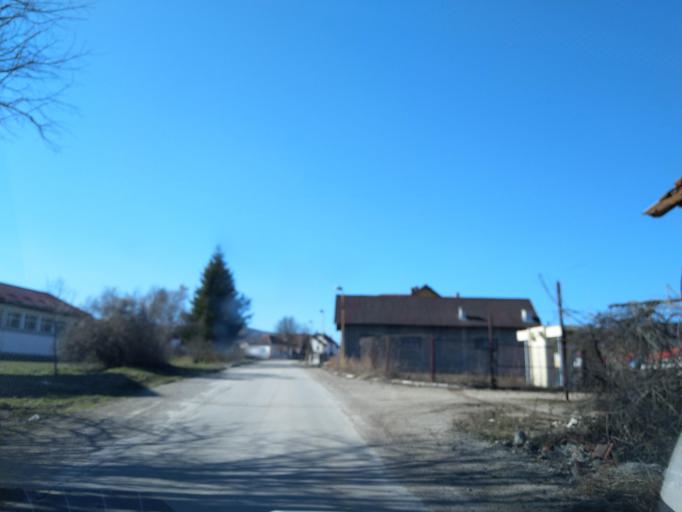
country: RS
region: Central Serbia
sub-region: Zlatiborski Okrug
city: Kosjeric
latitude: 43.9395
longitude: 19.8740
